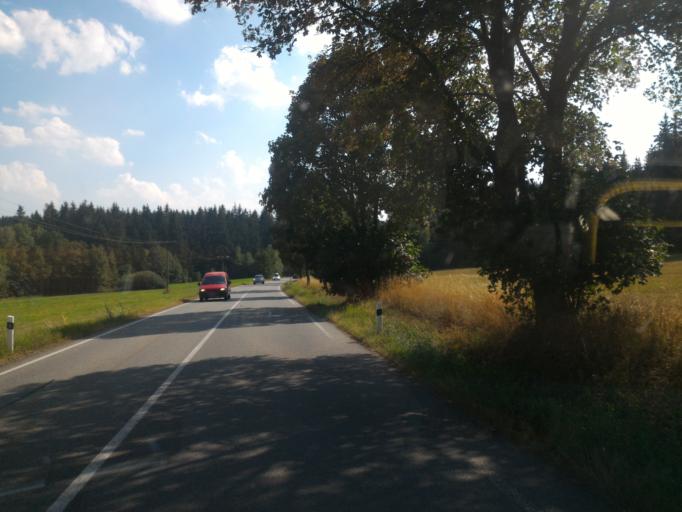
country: CZ
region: Vysocina
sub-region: Okres Jihlava
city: Trest'
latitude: 49.2568
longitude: 15.4716
